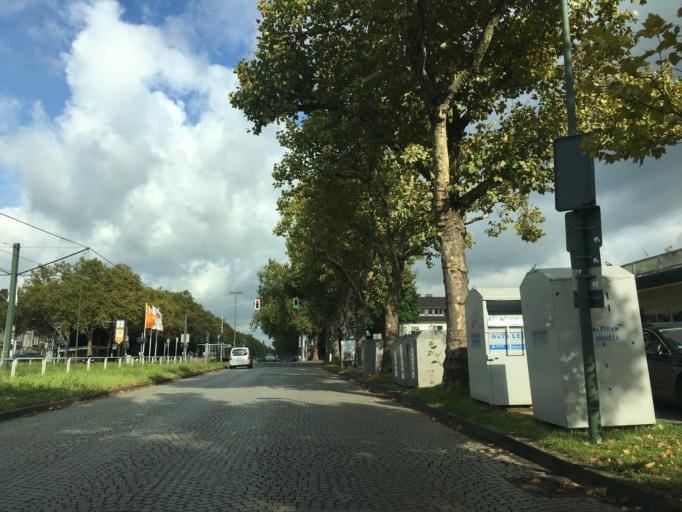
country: DE
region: North Rhine-Westphalia
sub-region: Regierungsbezirk Dusseldorf
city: Dusseldorf
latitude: 51.2591
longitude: 6.7550
